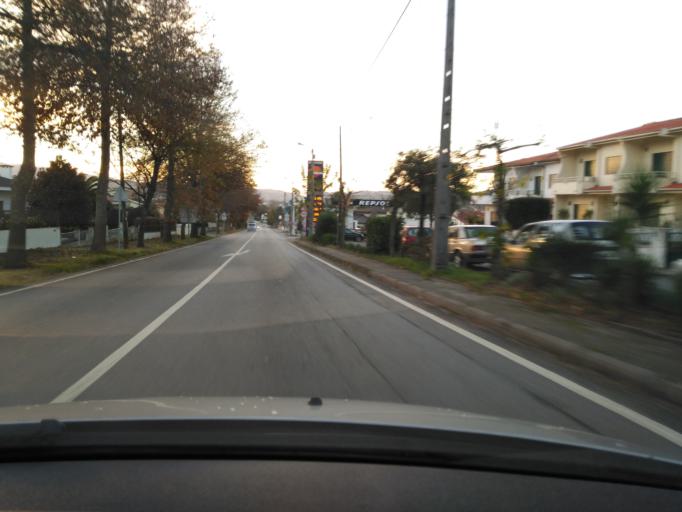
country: PT
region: Braga
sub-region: Guimaraes
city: Brito
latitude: 41.4949
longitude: -8.3625
